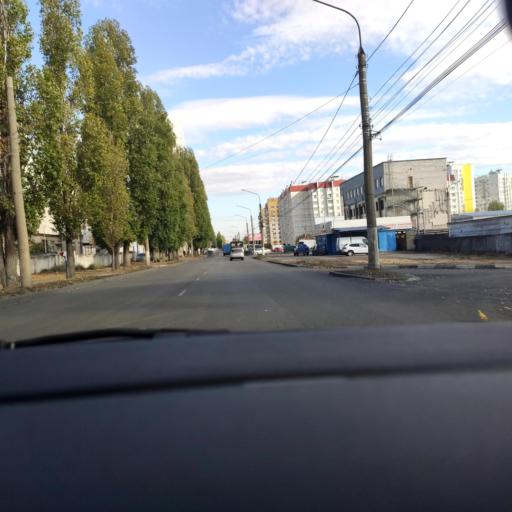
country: RU
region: Voronezj
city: Podgornoye
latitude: 51.6933
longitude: 39.1409
